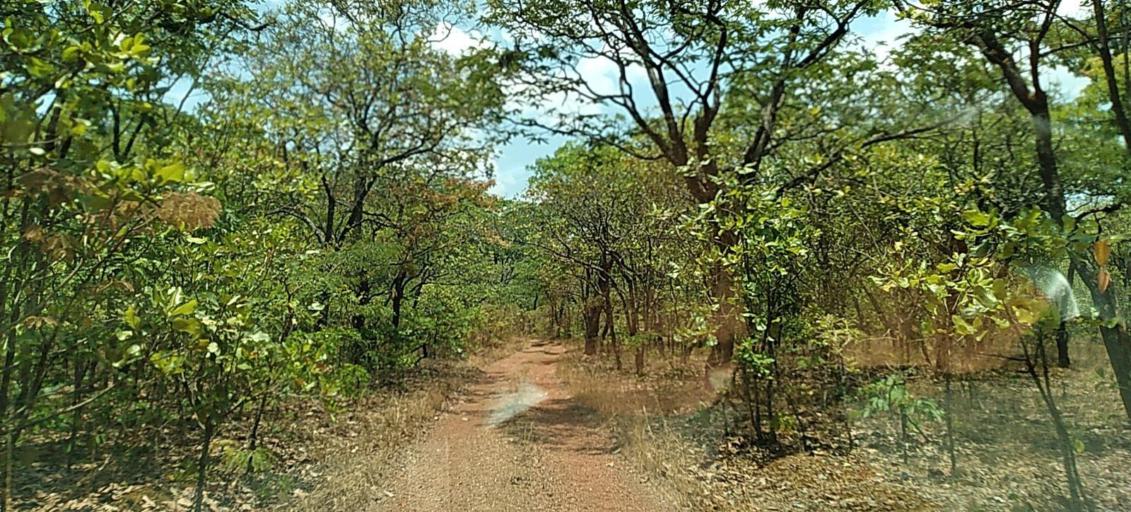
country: ZM
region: Copperbelt
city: Chililabombwe
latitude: -12.4549
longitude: 27.6978
